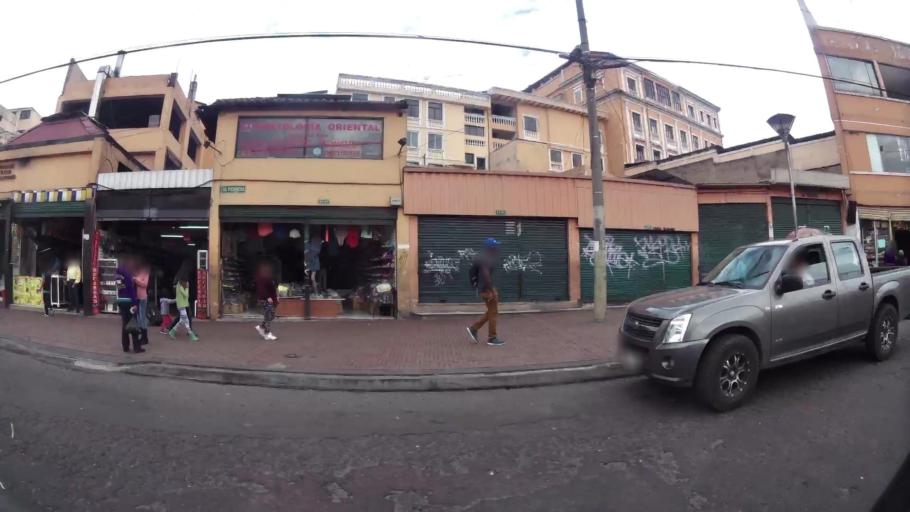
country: EC
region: Pichincha
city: Quito
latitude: -0.2224
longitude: -78.5086
